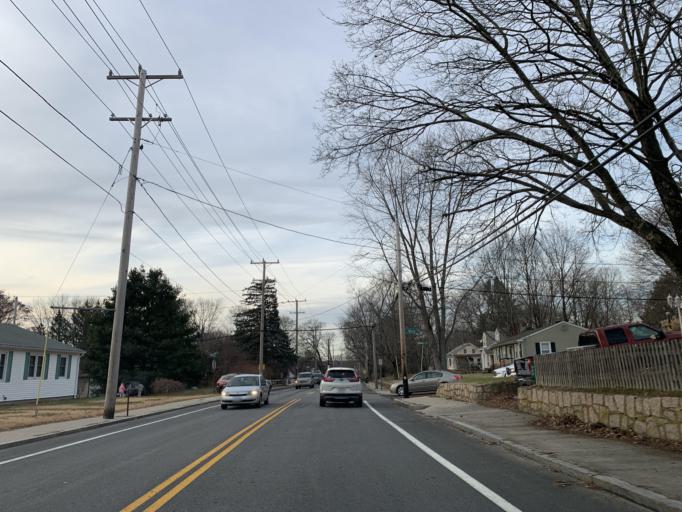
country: US
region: Rhode Island
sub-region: Providence County
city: Greenville
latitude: 41.8669
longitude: -71.5480
